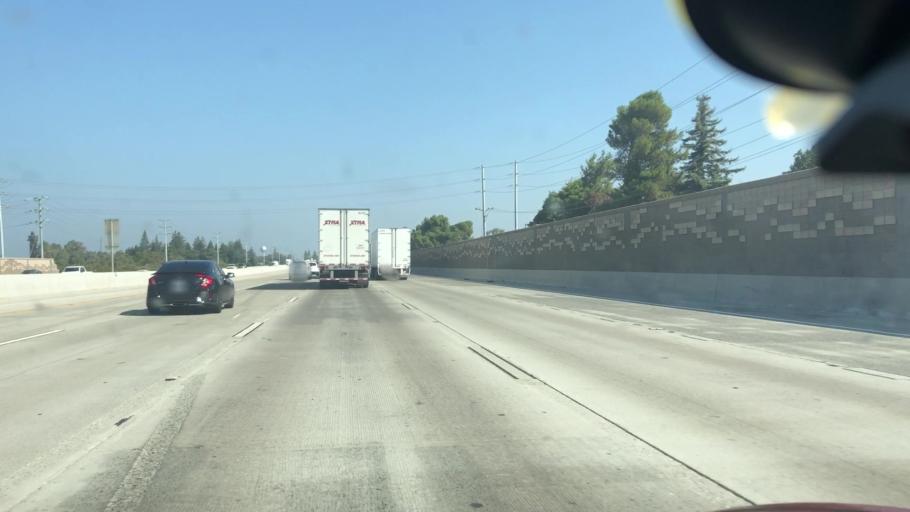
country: US
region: California
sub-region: San Joaquin County
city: Country Club
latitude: 37.9908
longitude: -121.3457
